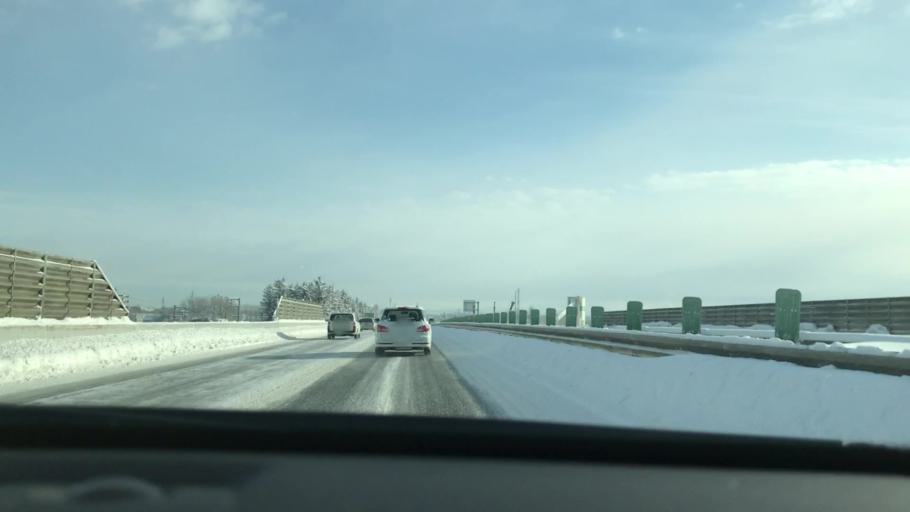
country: JP
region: Hokkaido
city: Sapporo
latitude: 43.0846
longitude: 141.4431
